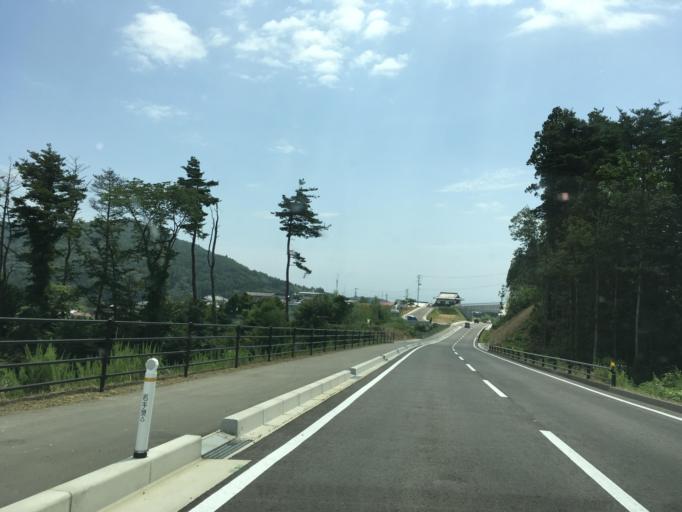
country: JP
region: Iwate
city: Ofunato
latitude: 39.0128
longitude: 141.7106
